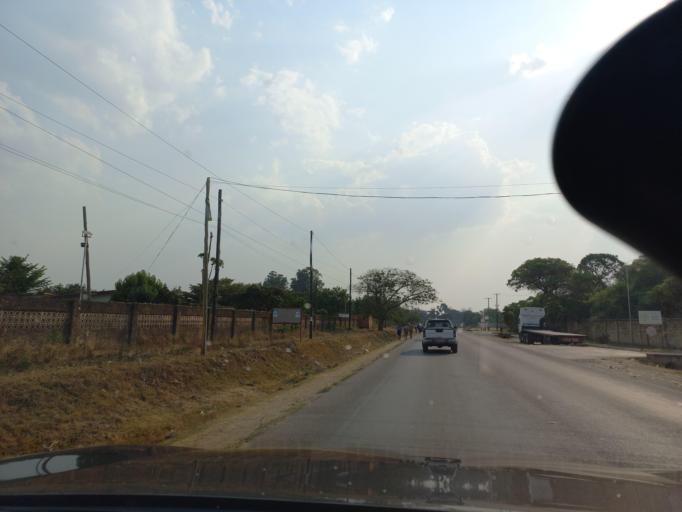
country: ZM
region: Lusaka
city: Lusaka
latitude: -15.4611
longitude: 28.2495
